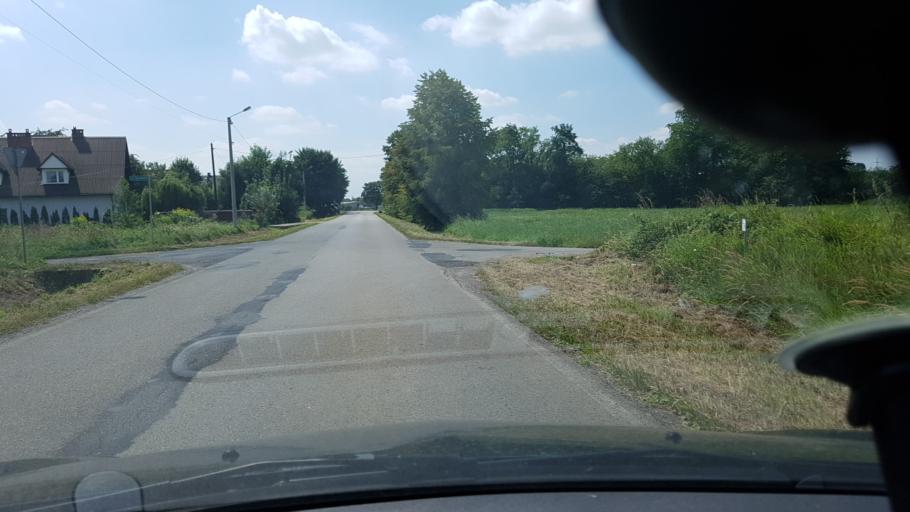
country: PL
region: Lesser Poland Voivodeship
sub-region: Powiat oswiecimski
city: Babice
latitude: 50.0551
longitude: 19.1905
